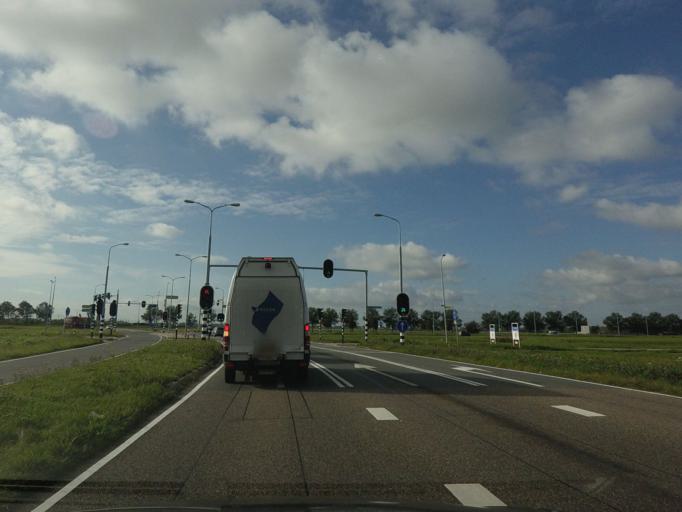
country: NL
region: North Holland
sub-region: Gemeente Haarlemmermeer
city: Hoofddorp
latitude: 52.2811
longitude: 4.6724
